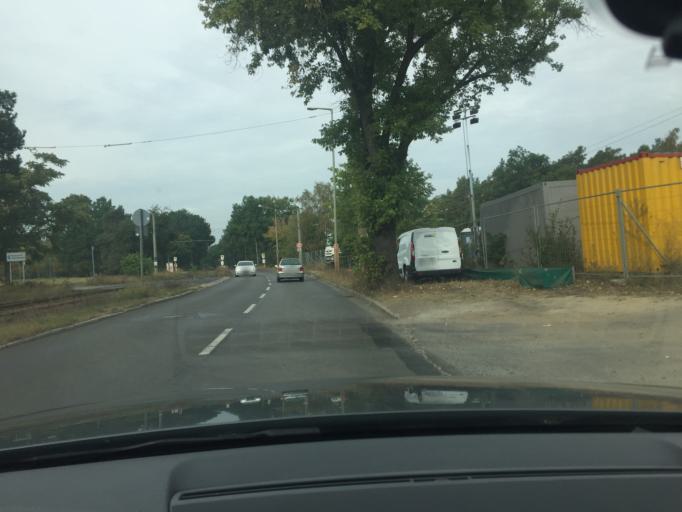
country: DE
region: Berlin
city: Friedrichshagen
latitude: 52.4559
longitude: 13.6438
